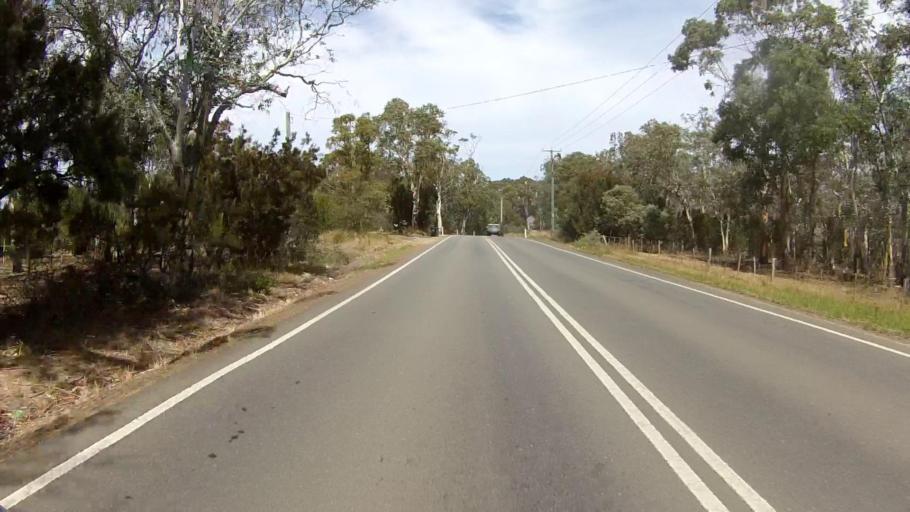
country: AU
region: Tasmania
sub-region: Clarence
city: Sandford
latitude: -42.9741
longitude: 147.5040
